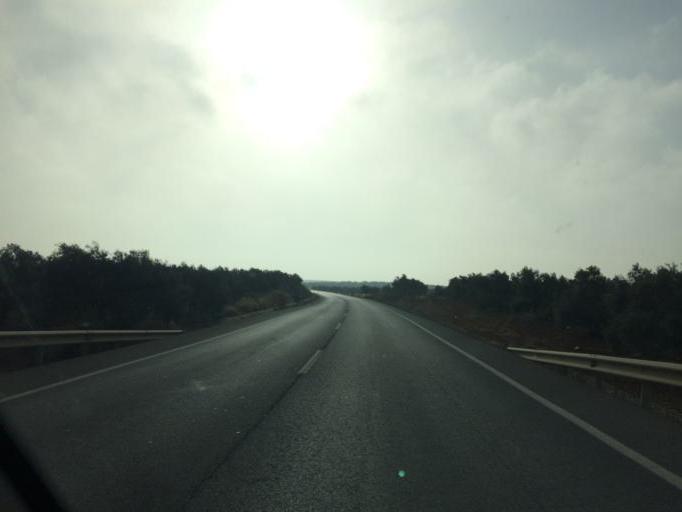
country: ES
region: Andalusia
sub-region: Provincia de Malaga
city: Campillos
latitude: 37.0477
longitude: -4.8350
